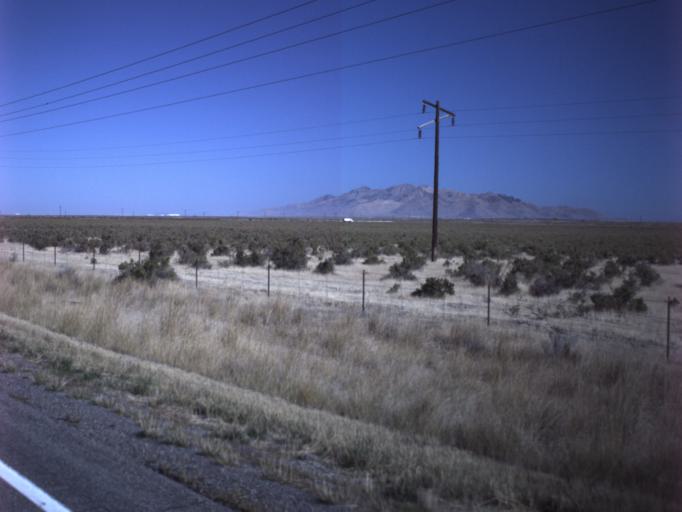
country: US
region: Utah
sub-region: Tooele County
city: Grantsville
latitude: 40.6718
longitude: -112.5477
